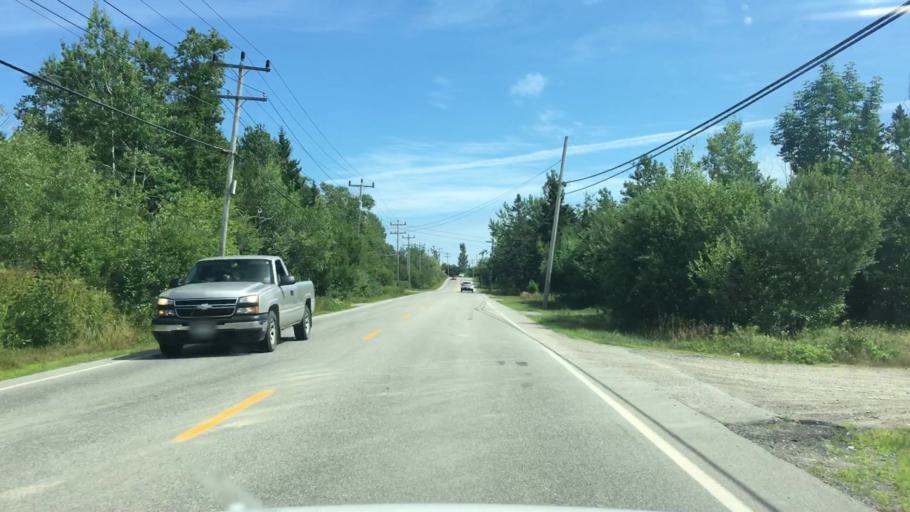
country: US
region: Maine
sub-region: Washington County
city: Eastport
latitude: 44.9172
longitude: -67.0114
